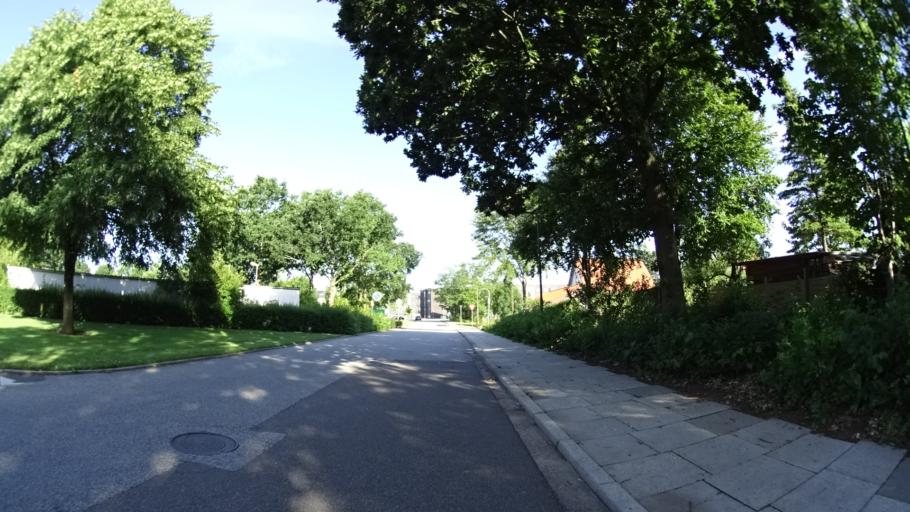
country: DK
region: Central Jutland
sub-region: Arhus Kommune
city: Stavtrup
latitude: 56.1175
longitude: 10.1583
